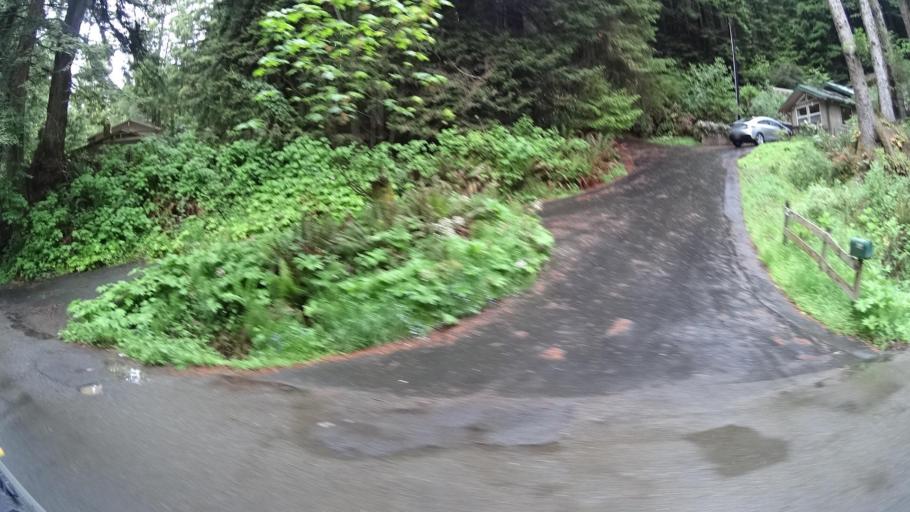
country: US
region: California
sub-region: Humboldt County
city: Bayside
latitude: 40.8220
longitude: -124.0328
